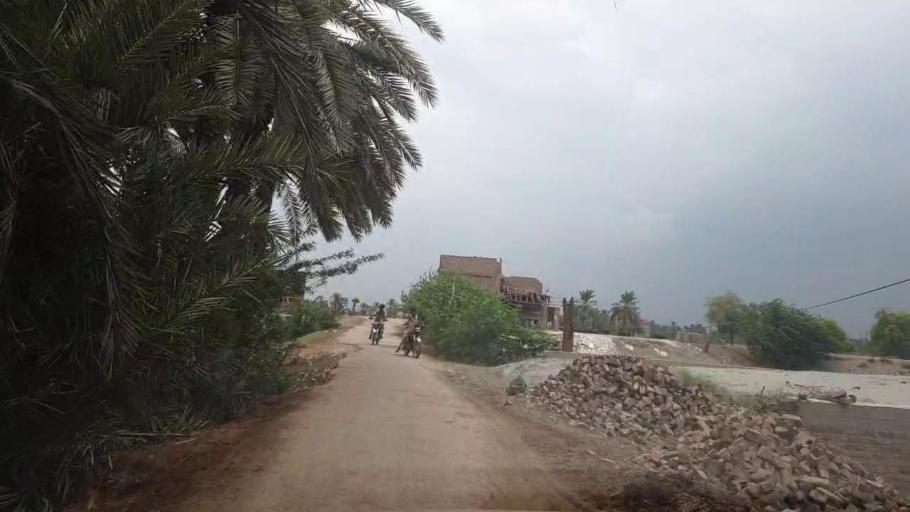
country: PK
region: Sindh
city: Khairpur
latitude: 27.5511
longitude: 68.7462
